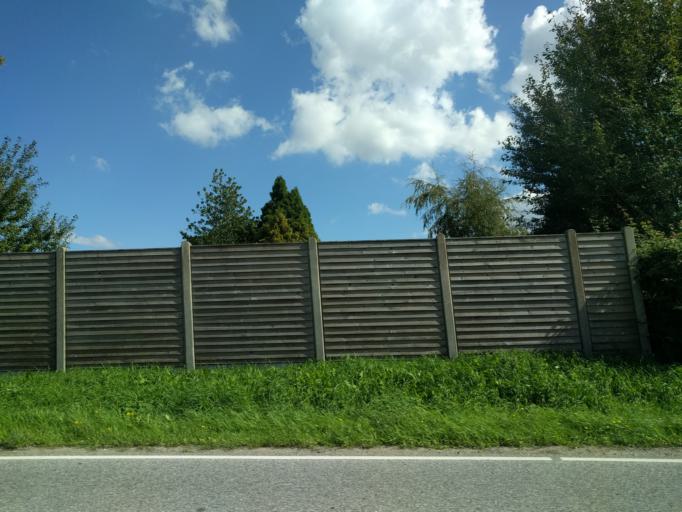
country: DK
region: Central Jutland
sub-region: Skive Kommune
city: Skive
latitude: 56.5883
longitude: 9.0294
